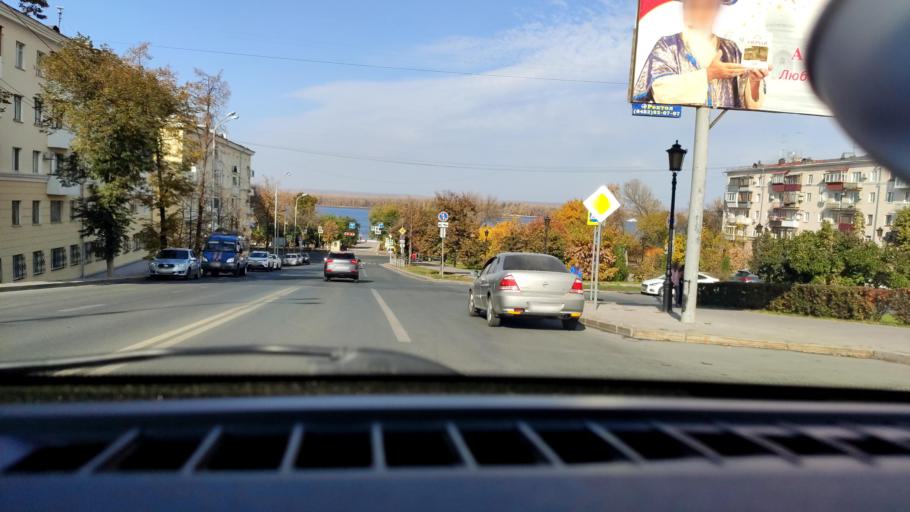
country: RU
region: Samara
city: Samara
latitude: 53.2084
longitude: 50.1198
